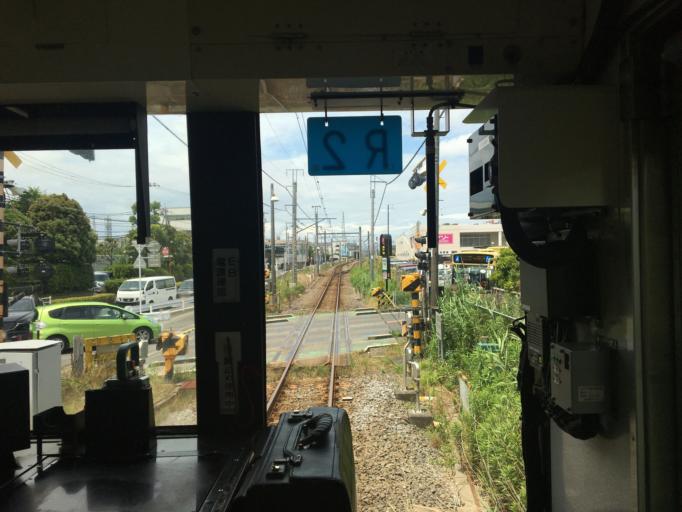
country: JP
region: Kanagawa
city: Chigasaki
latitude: 35.3364
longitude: 139.4093
